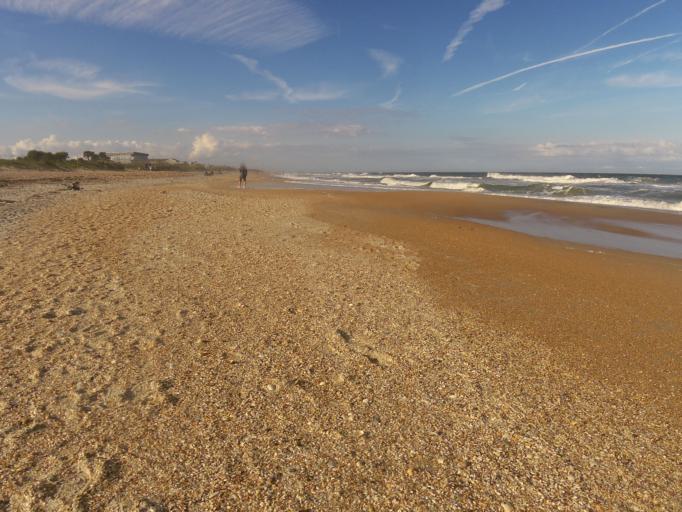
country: US
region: Florida
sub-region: Saint Johns County
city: Villano Beach
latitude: 29.9151
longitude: -81.2891
